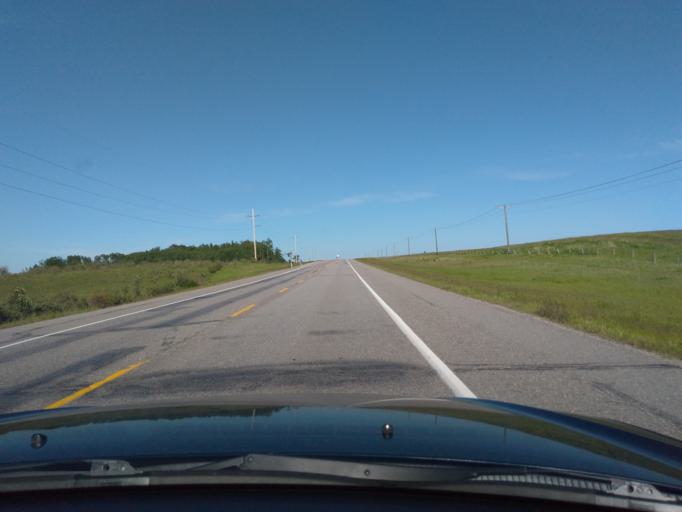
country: CA
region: Alberta
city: Cochrane
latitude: 51.0233
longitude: -114.4483
